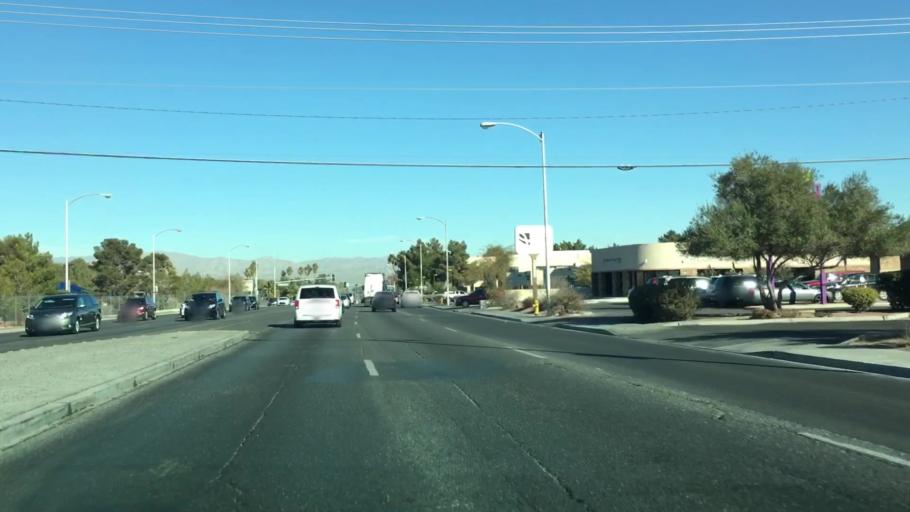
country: US
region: Nevada
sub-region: Clark County
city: Winchester
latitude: 36.1163
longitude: -115.1191
